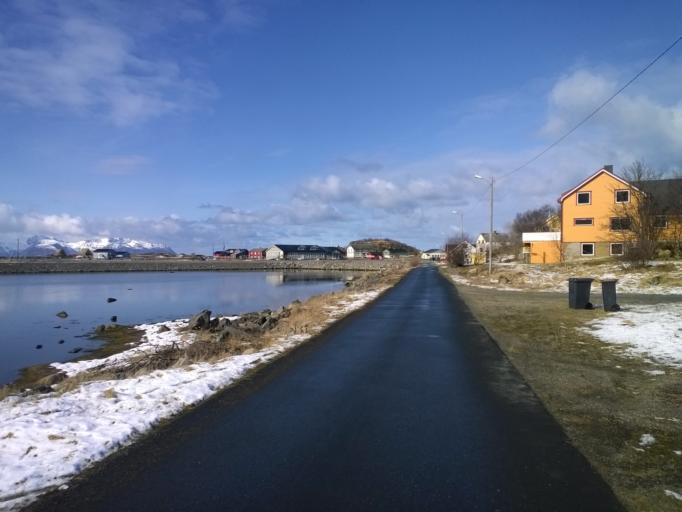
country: NO
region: Nordland
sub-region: Vagan
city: Kabelvag
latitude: 68.3873
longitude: 14.4232
